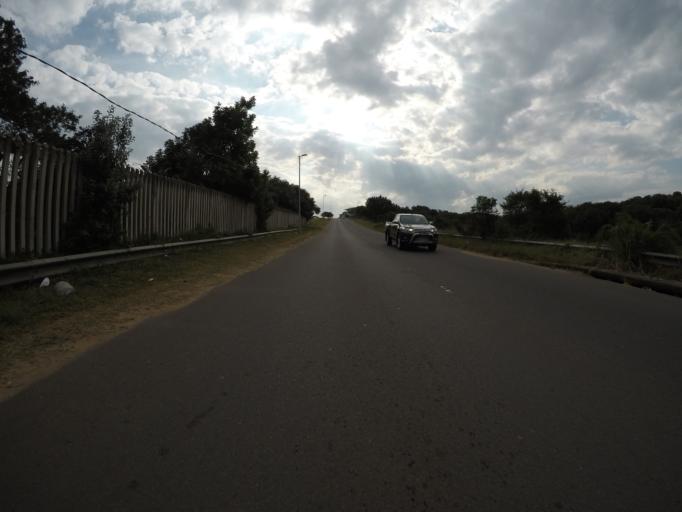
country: ZA
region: KwaZulu-Natal
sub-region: uThungulu District Municipality
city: Richards Bay
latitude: -28.7446
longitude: 32.0837
